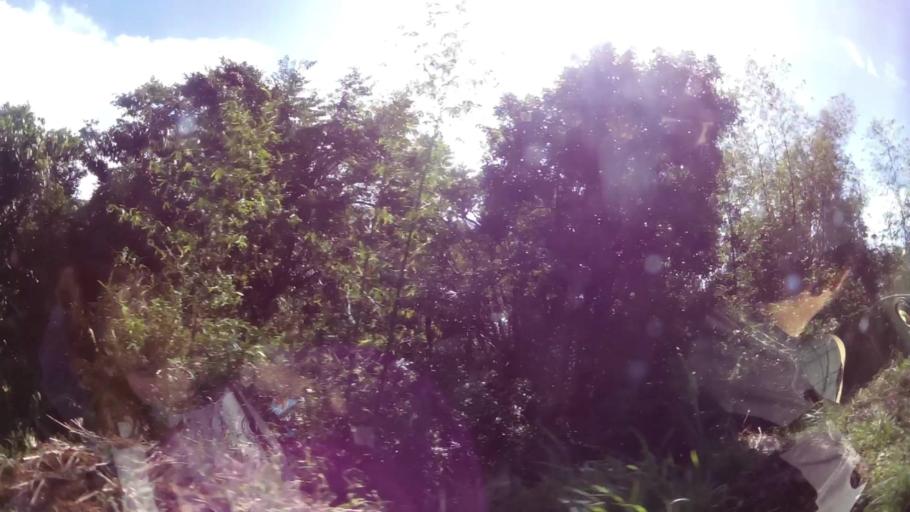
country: DM
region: Saint Paul
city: Pont Casse
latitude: 15.3567
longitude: -61.3567
